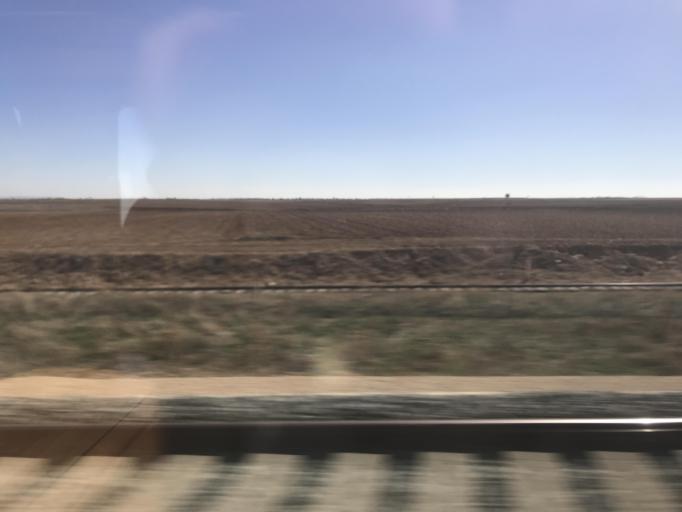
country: ES
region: Castille-La Mancha
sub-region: Province of Toledo
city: Santa Cruz de la Zarza
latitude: 39.9605
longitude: -3.2146
